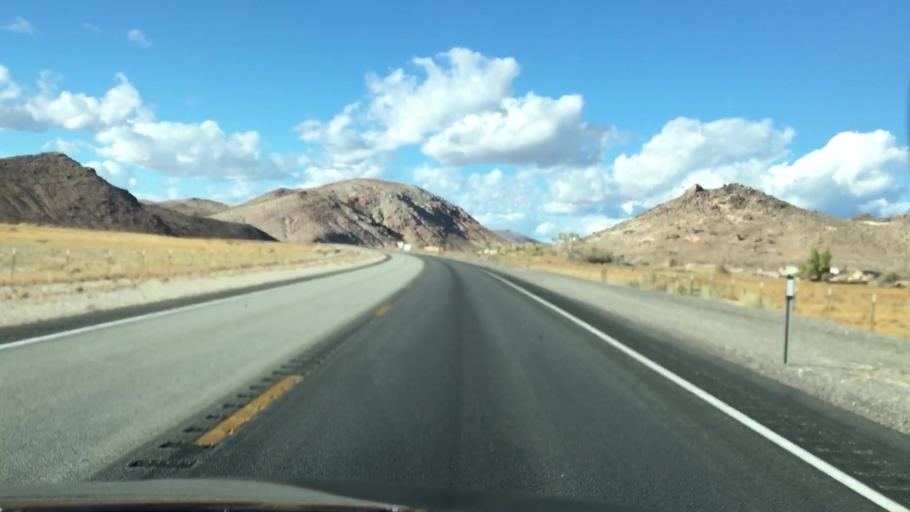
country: US
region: Nevada
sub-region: Nye County
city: Beatty
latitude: 36.9679
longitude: -116.7194
